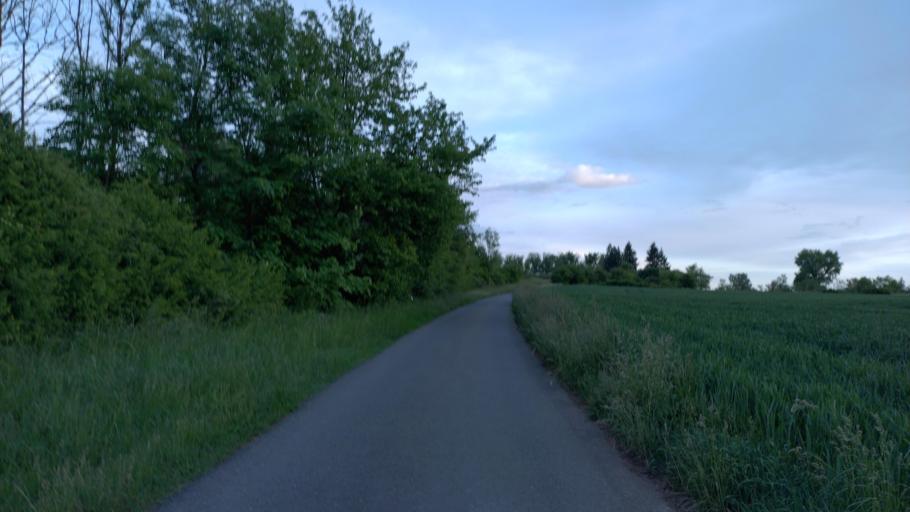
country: DE
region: Bavaria
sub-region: Upper Franconia
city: Bindlach
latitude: 49.9979
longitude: 11.6176
